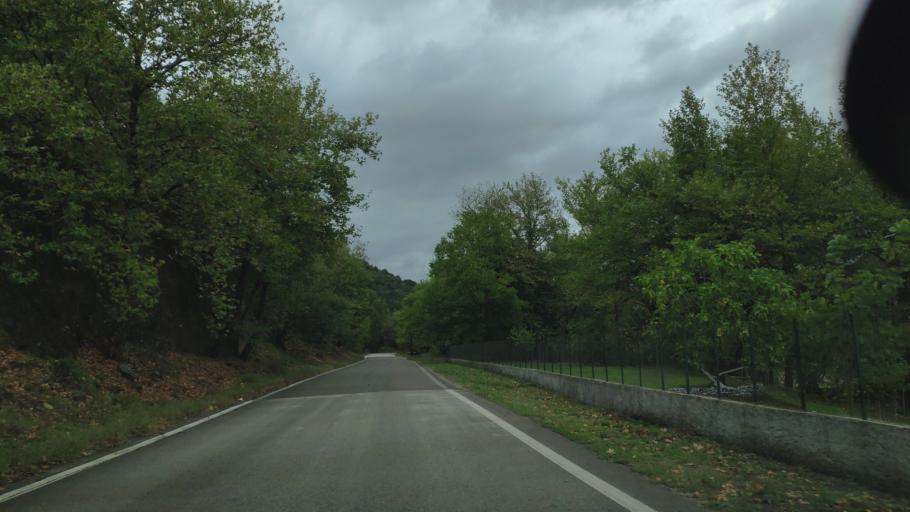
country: GR
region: West Greece
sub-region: Nomos Aitolias kai Akarnanias
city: Sardinia
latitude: 38.9522
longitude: 21.3404
